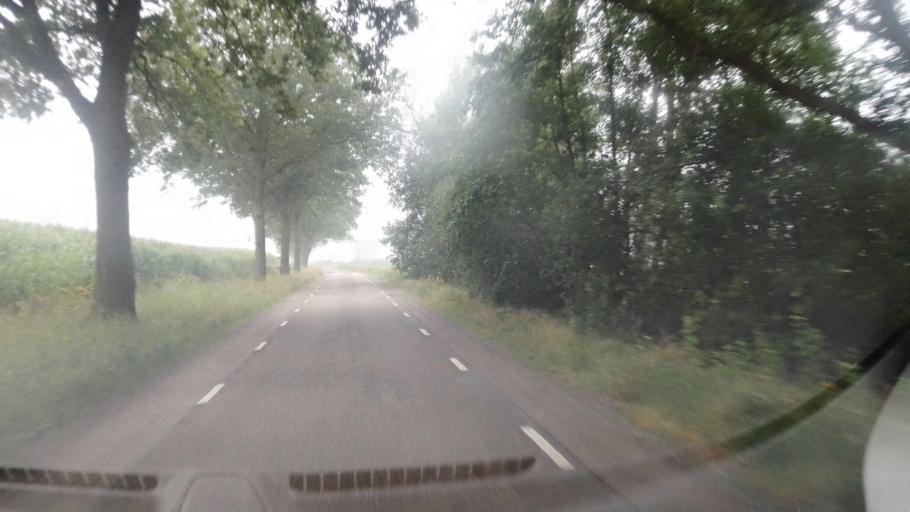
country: NL
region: Limburg
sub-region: Gemeente Peel en Maas
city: Maasbree
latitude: 51.4322
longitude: 6.0115
